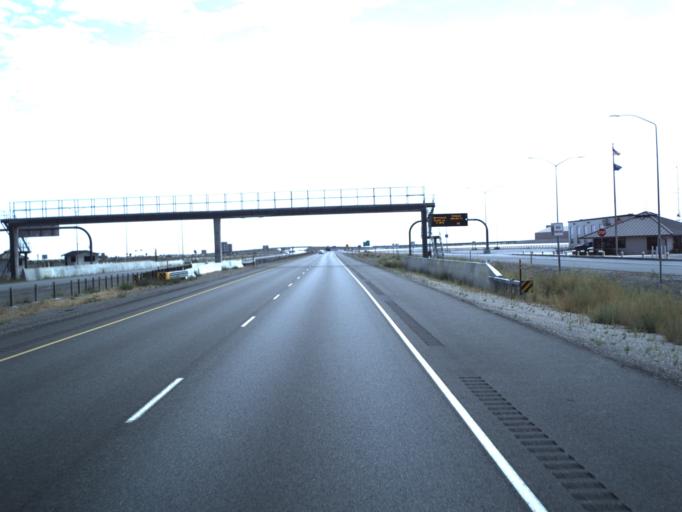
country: US
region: Utah
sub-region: Tooele County
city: Wendover
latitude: 40.7453
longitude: -113.9918
